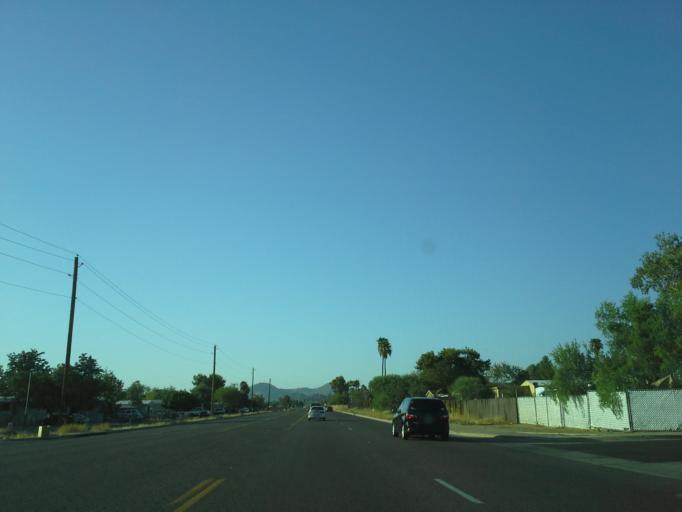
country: US
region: Arizona
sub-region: Pinal County
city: Apache Junction
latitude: 33.4091
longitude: -111.6327
